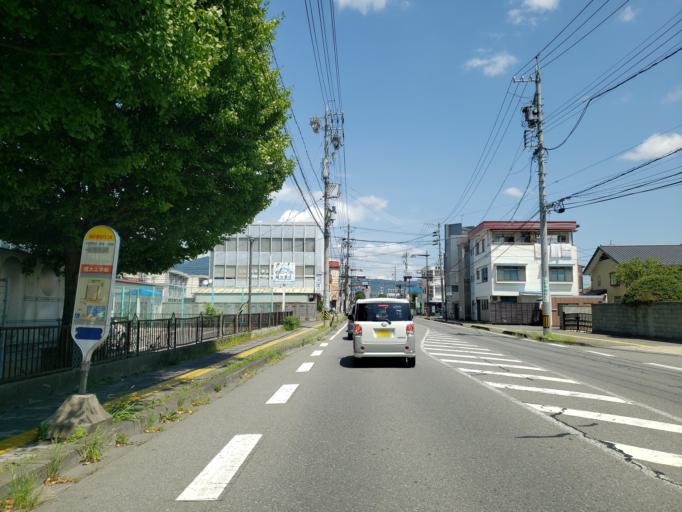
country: JP
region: Nagano
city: Nagano-shi
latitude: 36.6311
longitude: 138.1910
